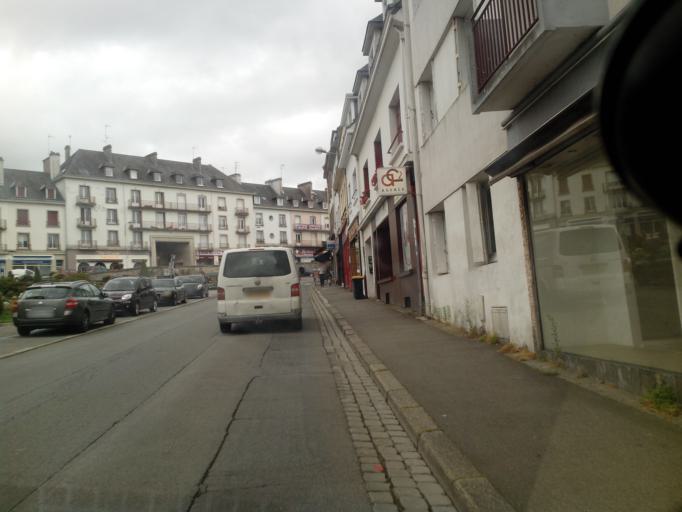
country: FR
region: Brittany
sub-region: Departement du Morbihan
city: Hennebont
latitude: 47.8050
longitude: -3.2786
